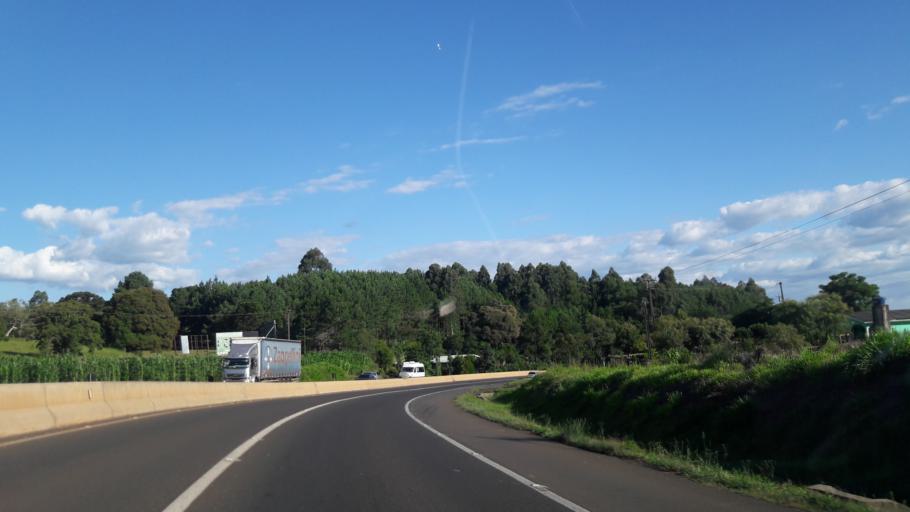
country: BR
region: Parana
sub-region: Guarapuava
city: Guarapuava
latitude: -25.3445
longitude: -51.3925
